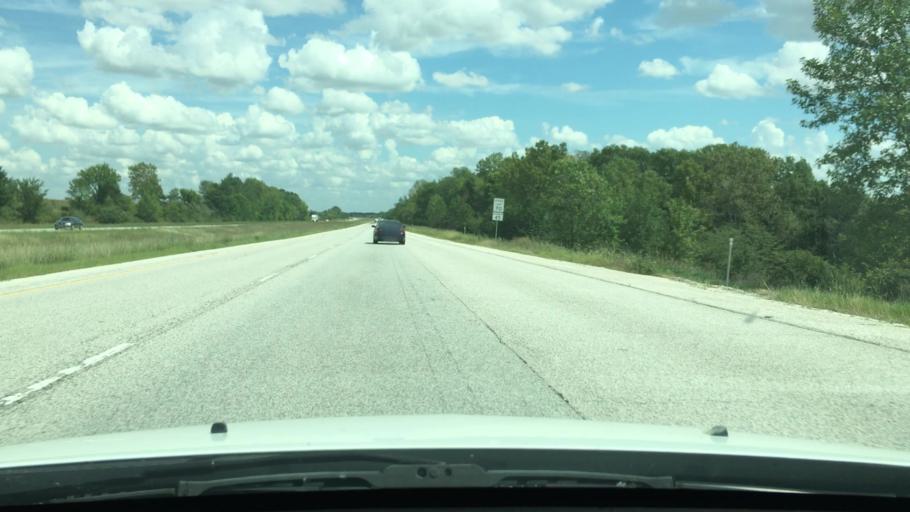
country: US
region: Illinois
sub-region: Morgan County
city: South Jacksonville
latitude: 39.6802
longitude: -90.2871
